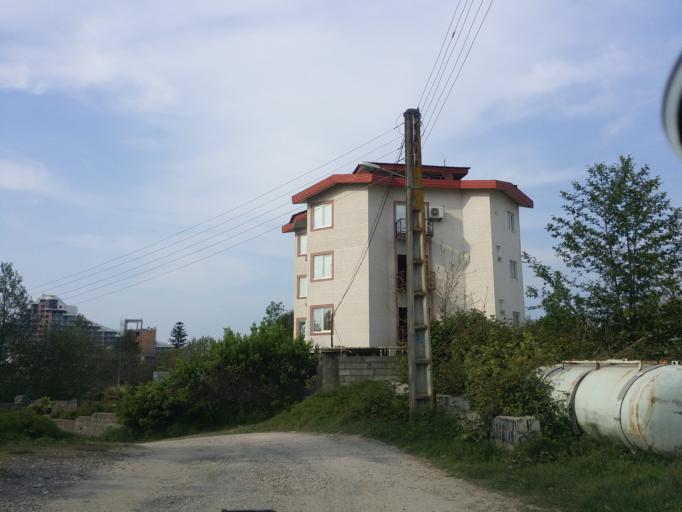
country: IR
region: Mazandaran
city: Chalus
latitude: 36.6840
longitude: 51.3966
